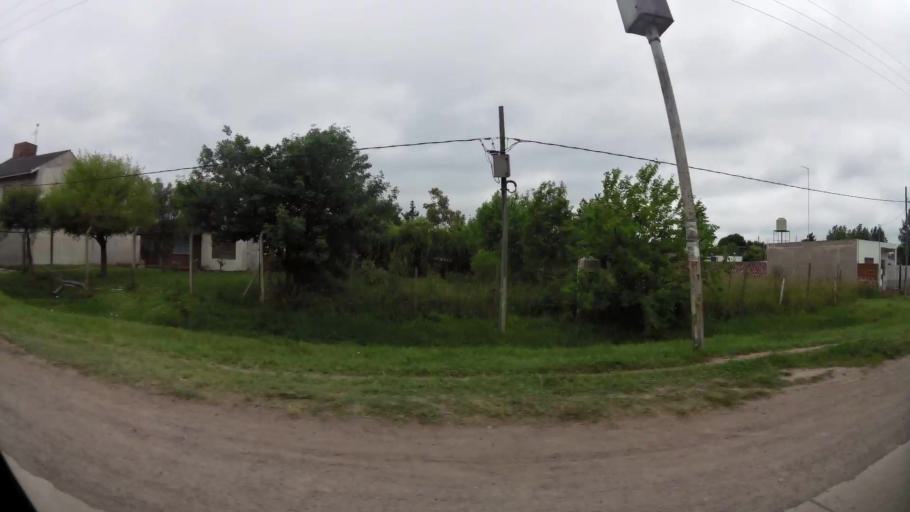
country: AR
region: Buenos Aires
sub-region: Partido de La Plata
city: La Plata
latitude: -35.0239
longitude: -58.0795
